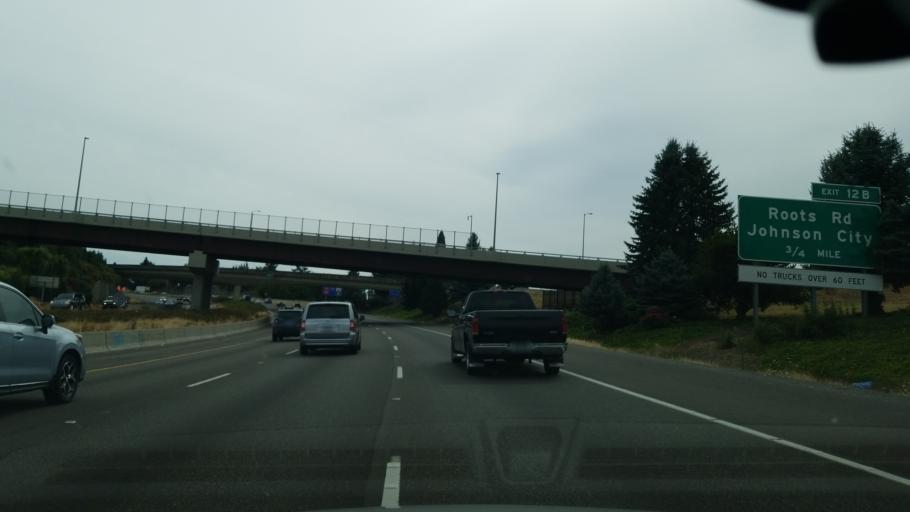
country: US
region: Oregon
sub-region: Clackamas County
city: Clackamas
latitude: 45.4195
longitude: -122.5737
